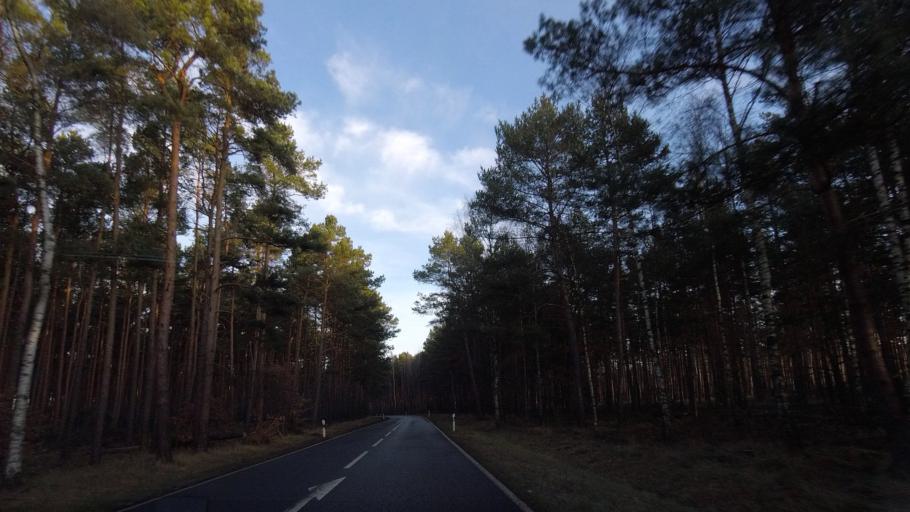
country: DE
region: Brandenburg
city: Niedergorsdorf
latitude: 52.0236
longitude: 12.9489
